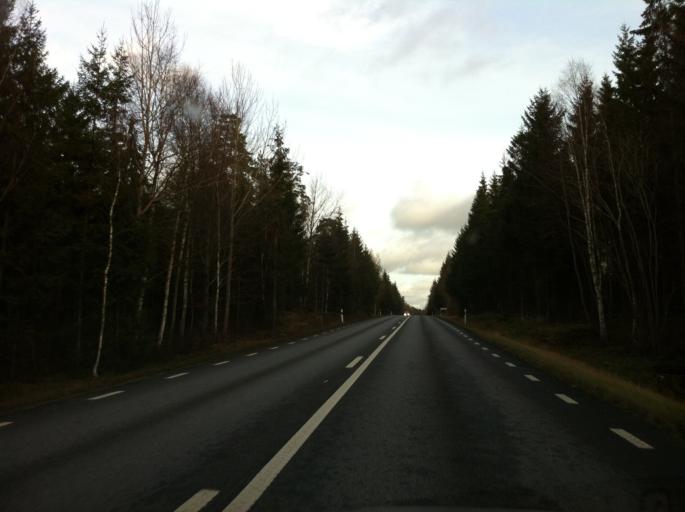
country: SE
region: Kronoberg
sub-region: Alvesta Kommun
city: Vislanda
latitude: 56.7597
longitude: 14.5234
